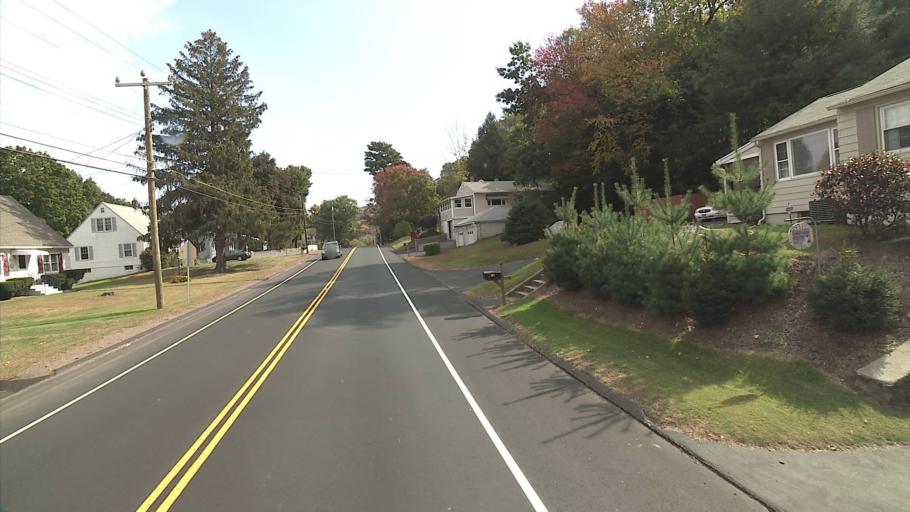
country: US
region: Connecticut
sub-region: Litchfield County
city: Thomaston
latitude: 41.6572
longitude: -73.0844
